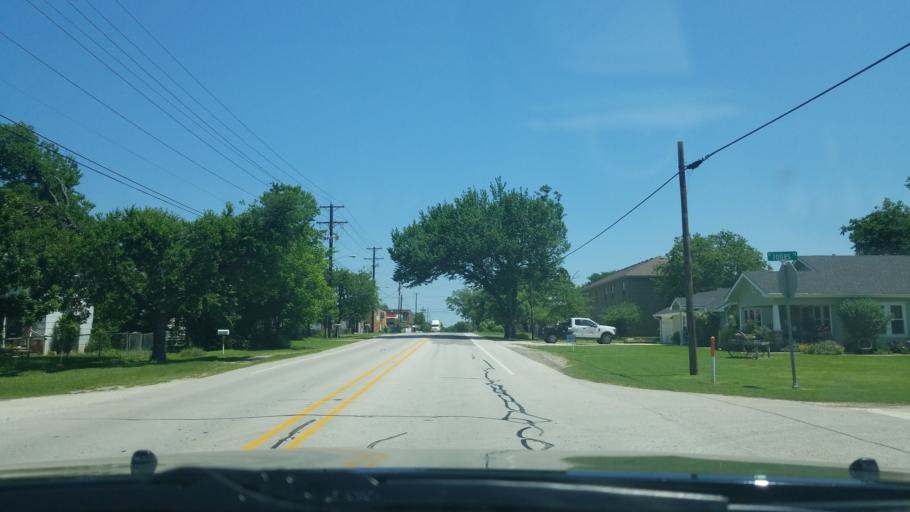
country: US
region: Texas
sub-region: Denton County
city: Krum
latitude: 33.2597
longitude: -97.2391
